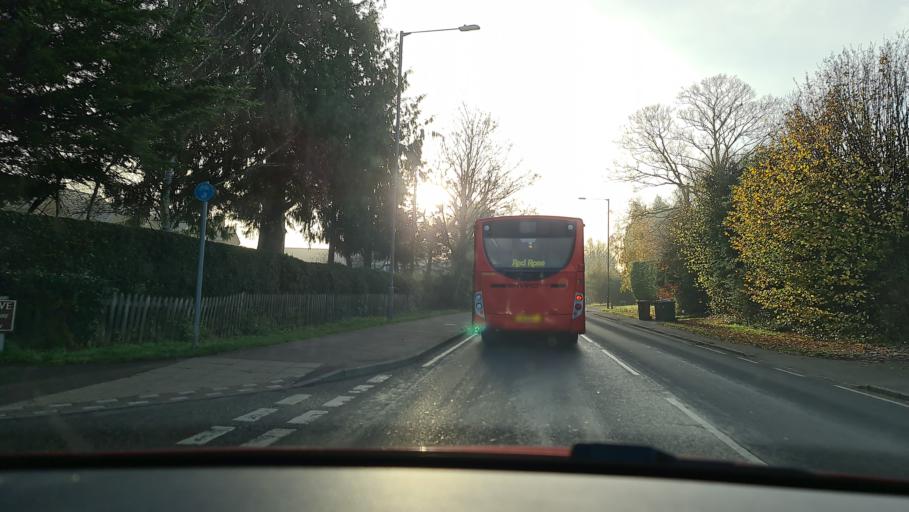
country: GB
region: England
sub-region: Buckinghamshire
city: Wendover
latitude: 51.7700
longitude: -0.7467
